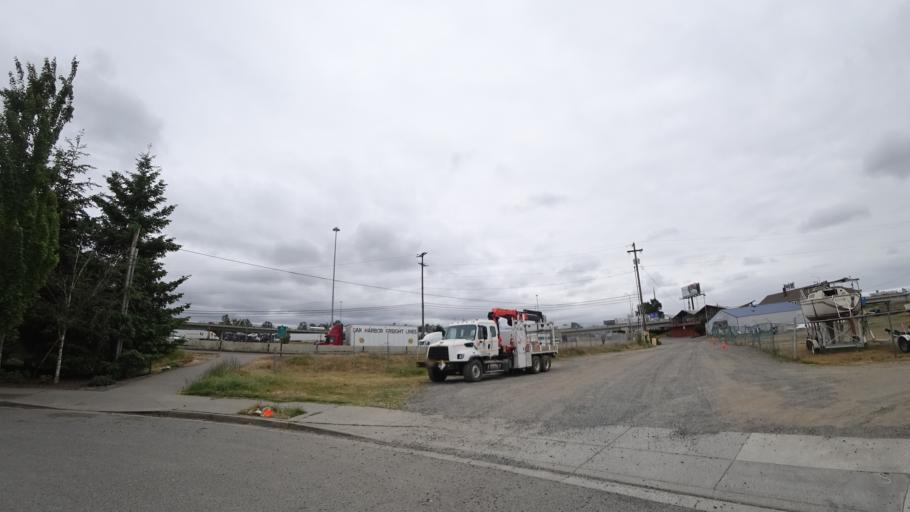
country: US
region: Washington
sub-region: Clark County
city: Vancouver
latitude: 45.6048
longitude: -122.6800
